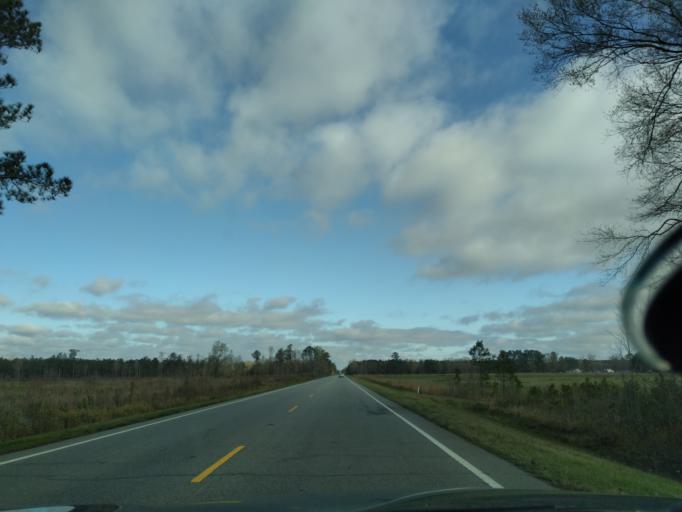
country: US
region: North Carolina
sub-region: Washington County
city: Plymouth
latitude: 35.9941
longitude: -76.7706
